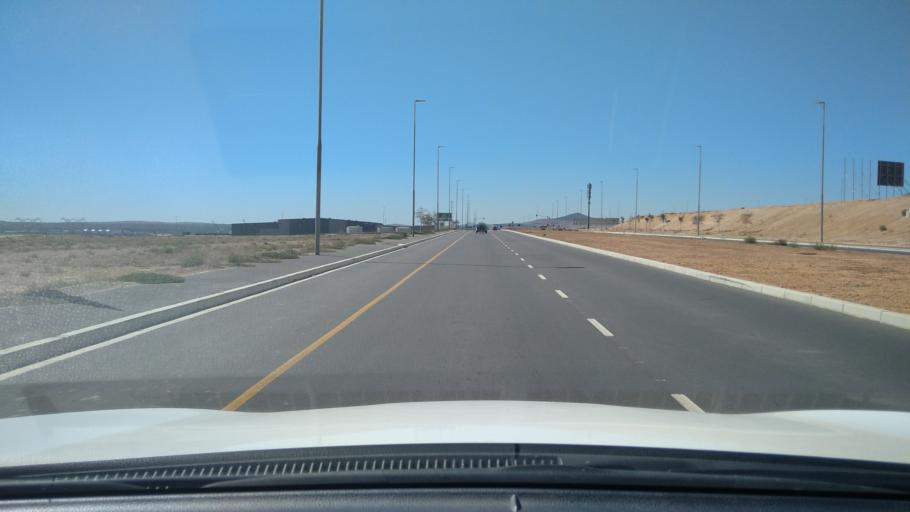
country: ZA
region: Western Cape
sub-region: City of Cape Town
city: Sunset Beach
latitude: -33.8213
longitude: 18.5523
